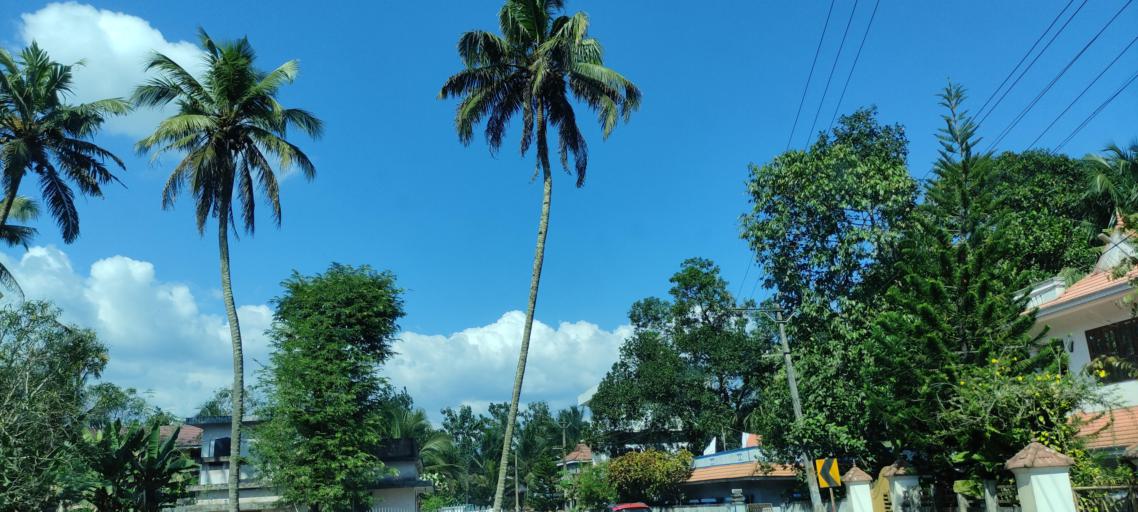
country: IN
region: Kerala
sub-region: Pattanamtitta
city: Adur
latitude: 9.1828
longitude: 76.7443
